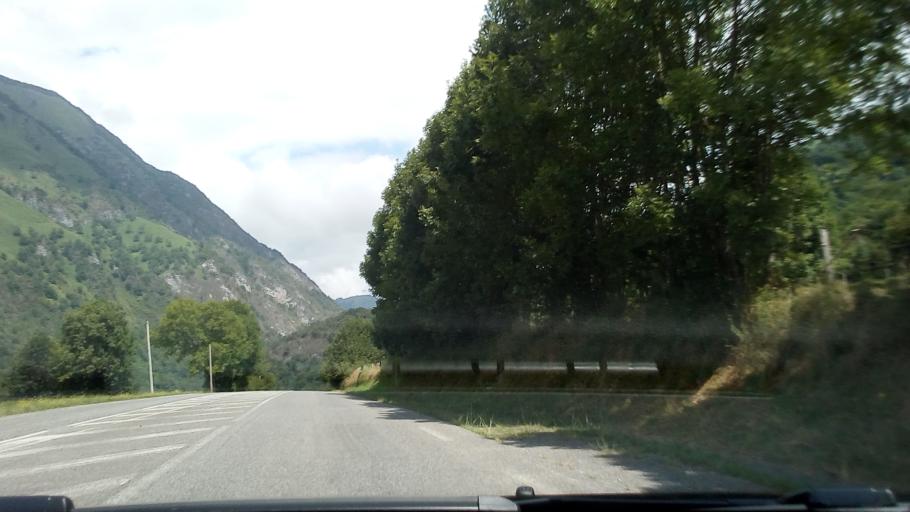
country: FR
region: Aquitaine
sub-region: Departement des Pyrenees-Atlantiques
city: Arette
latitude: 43.0057
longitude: -0.6011
